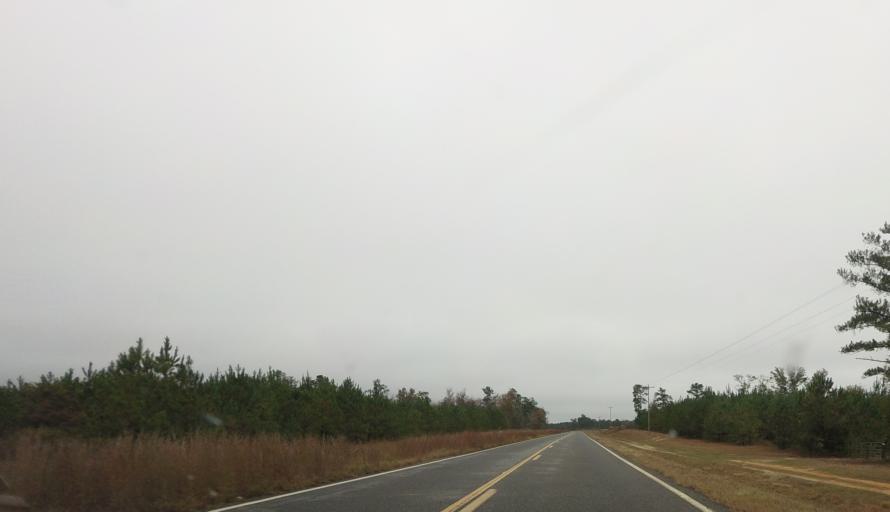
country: US
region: Georgia
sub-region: Taylor County
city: Butler
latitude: 32.4324
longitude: -84.3119
